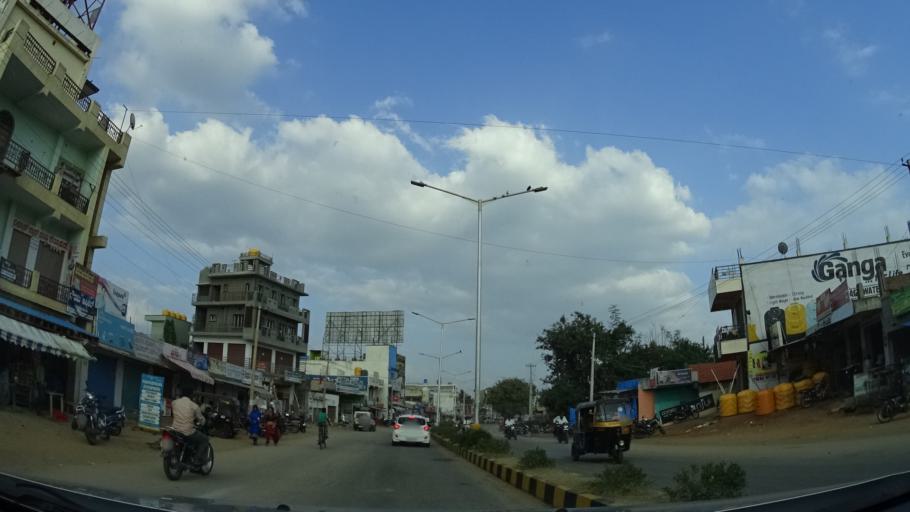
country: IN
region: Karnataka
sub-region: Mandya
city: Malavalli
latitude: 12.3848
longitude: 77.0534
